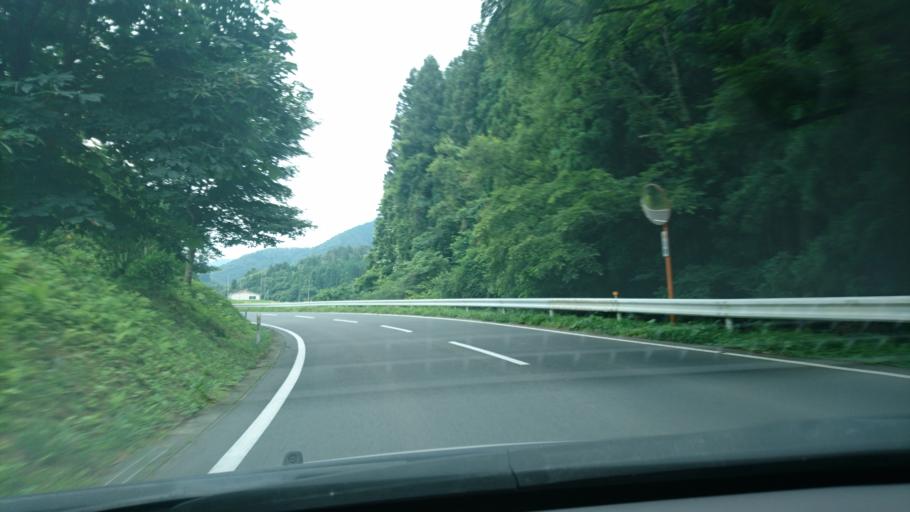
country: JP
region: Iwate
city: Ichinoseki
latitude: 38.8650
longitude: 141.4248
